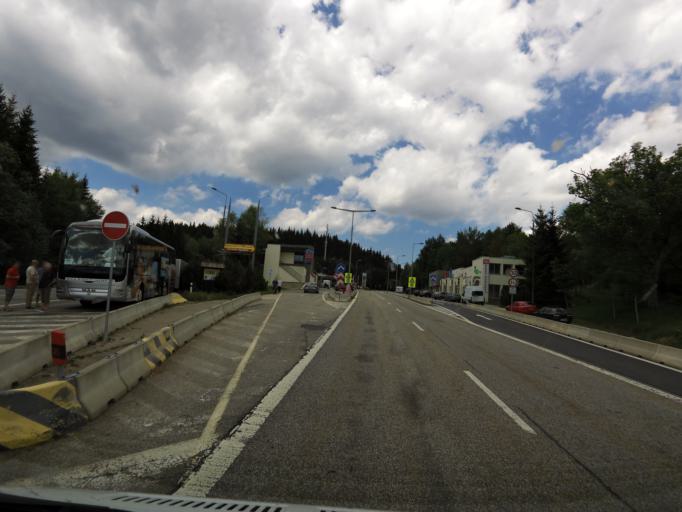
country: DE
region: Bavaria
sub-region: Lower Bavaria
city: Philippsreut
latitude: 48.8833
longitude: 13.7046
